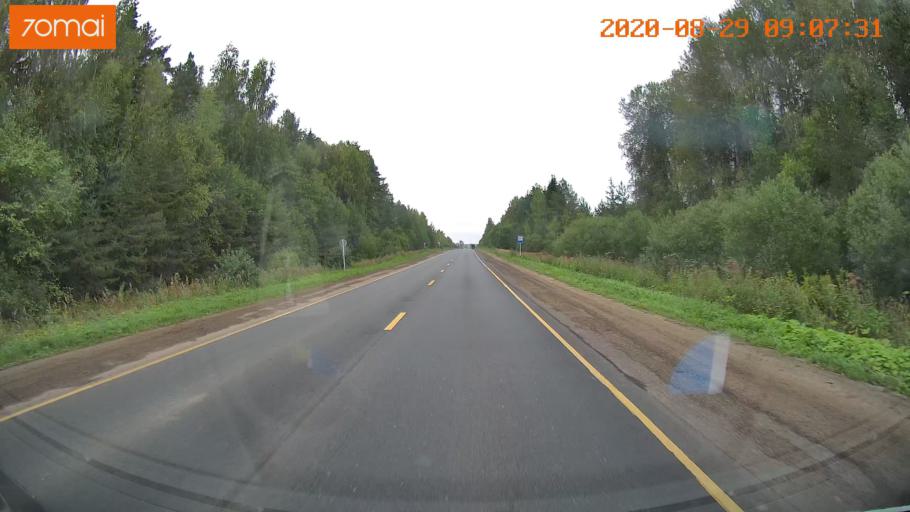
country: RU
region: Ivanovo
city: Navoloki
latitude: 57.3828
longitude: 42.0347
